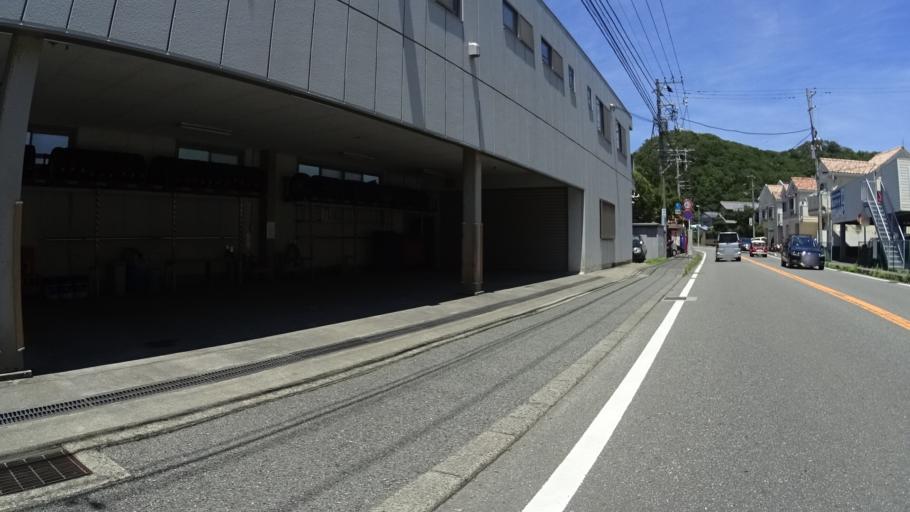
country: JP
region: Kanagawa
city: Hayama
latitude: 35.2790
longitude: 139.5794
